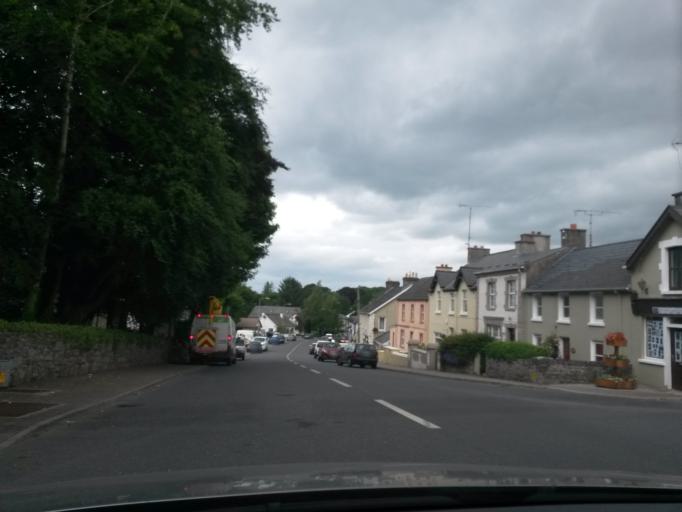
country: IE
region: Connaught
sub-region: County Leitrim
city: Manorhamilton
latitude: 54.2287
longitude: -8.3006
